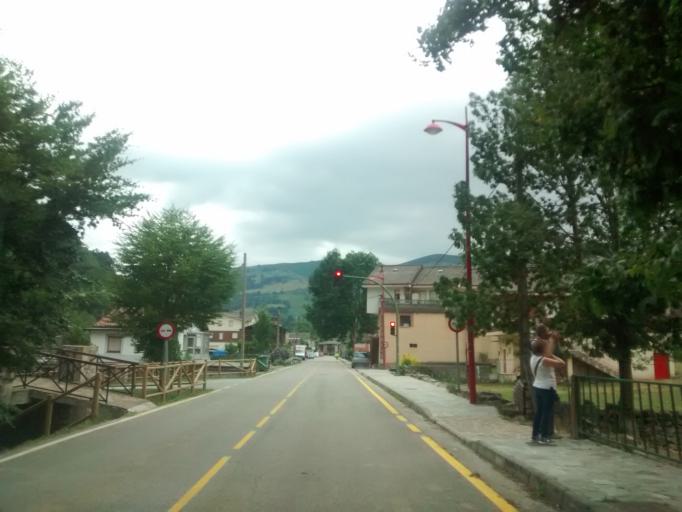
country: ES
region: Cantabria
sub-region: Provincia de Cantabria
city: Vega de Pas
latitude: 43.1541
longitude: -3.7809
